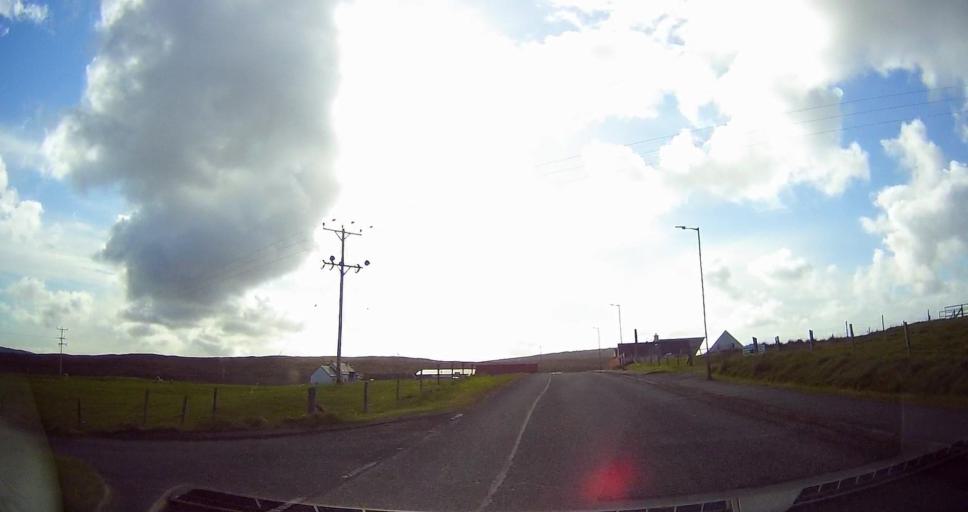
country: GB
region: Scotland
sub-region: Shetland Islands
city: Shetland
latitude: 60.3689
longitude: -1.1370
